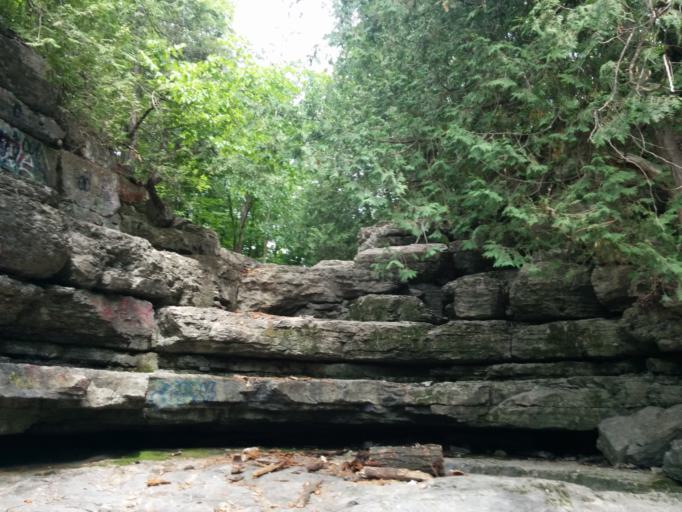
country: CA
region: Ontario
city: Clarence-Rockland
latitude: 45.4854
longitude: -75.4693
